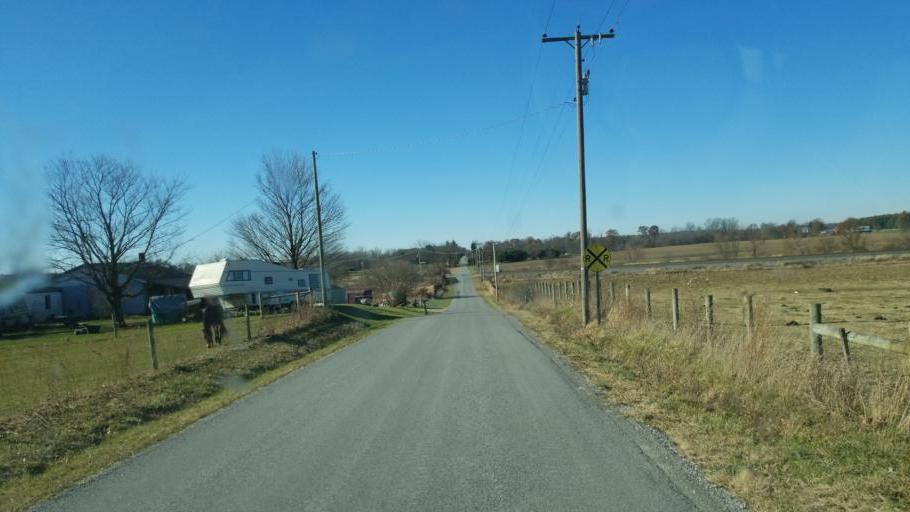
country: US
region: Ohio
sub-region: Huron County
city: Plymouth
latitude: 40.9745
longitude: -82.5926
